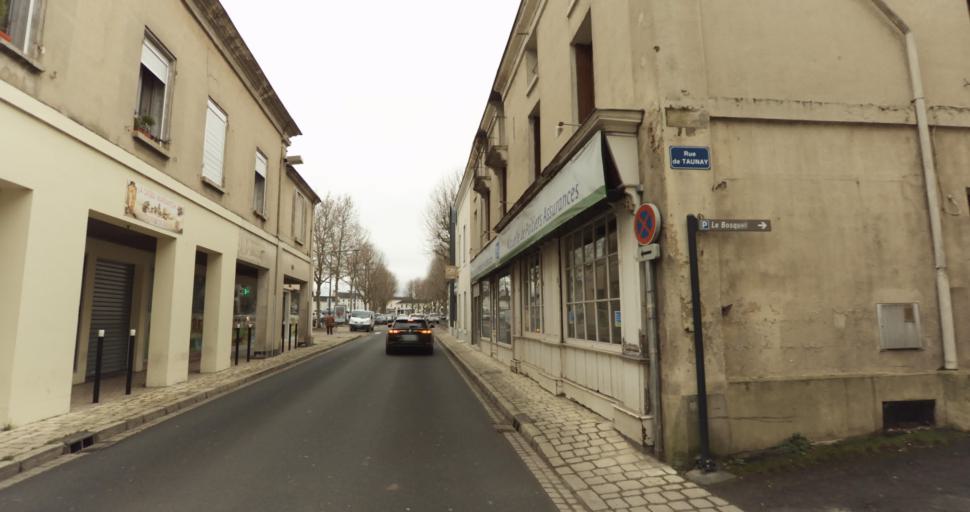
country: FR
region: Pays de la Loire
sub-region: Departement de Maine-et-Loire
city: Doue-la-Fontaine
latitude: 47.1933
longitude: -0.2763
